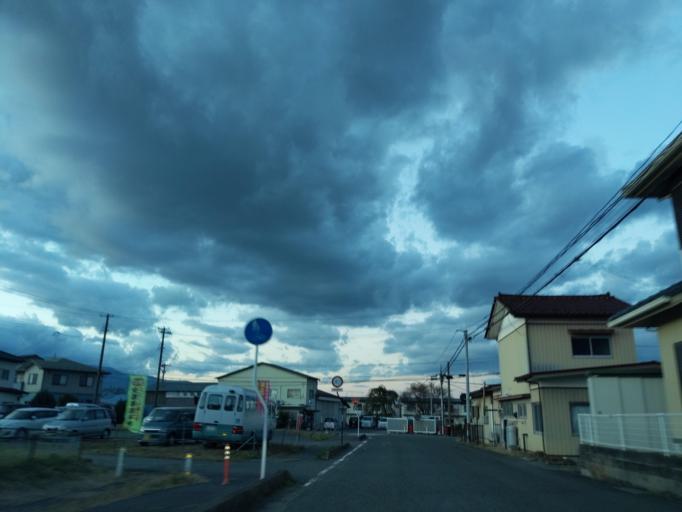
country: JP
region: Fukushima
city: Motomiya
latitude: 37.4959
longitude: 140.3895
